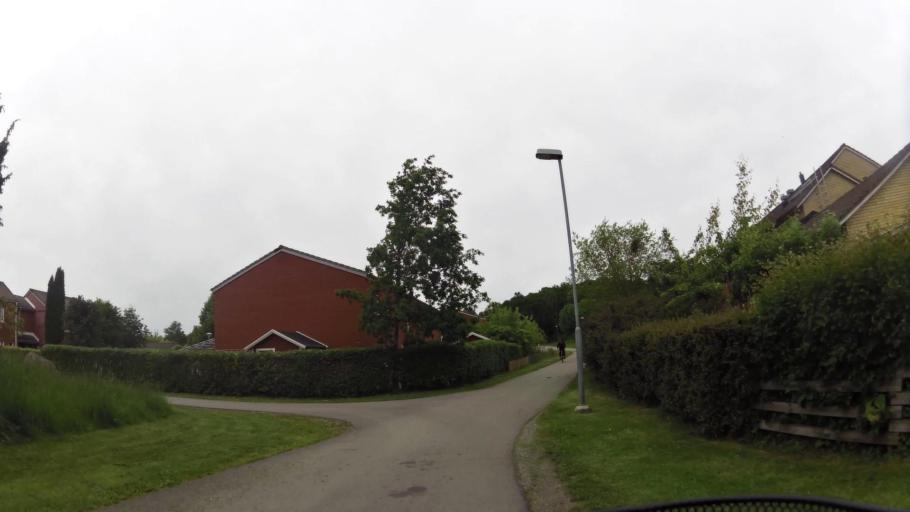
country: SE
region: OEstergoetland
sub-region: Linkopings Kommun
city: Malmslatt
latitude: 58.3840
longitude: 15.5671
